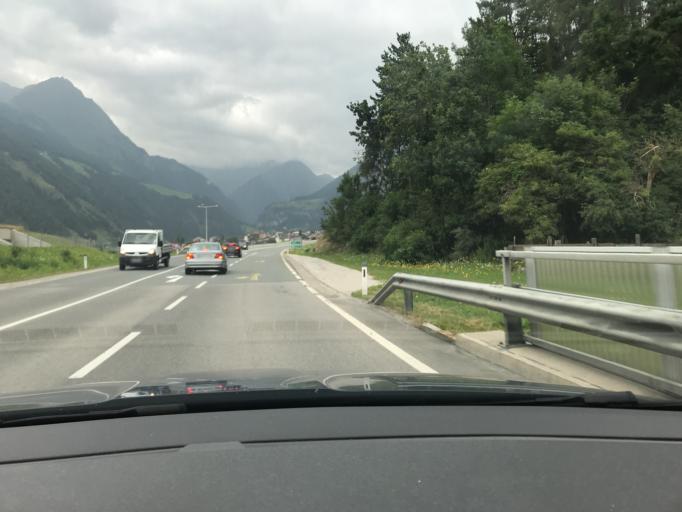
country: AT
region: Tyrol
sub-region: Politischer Bezirk Lienz
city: Matrei in Osttirol
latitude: 46.9906
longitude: 12.5442
